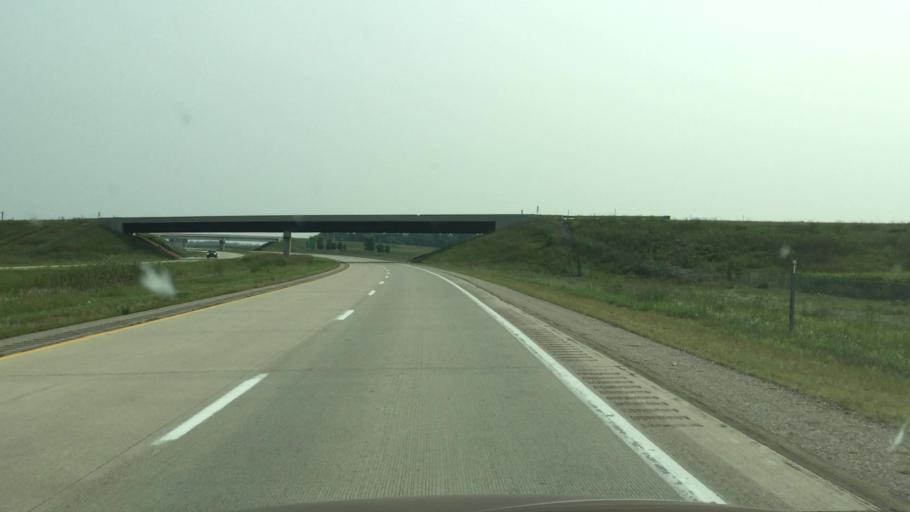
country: US
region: Iowa
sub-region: Osceola County
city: Sibley
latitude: 43.3864
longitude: -95.7238
